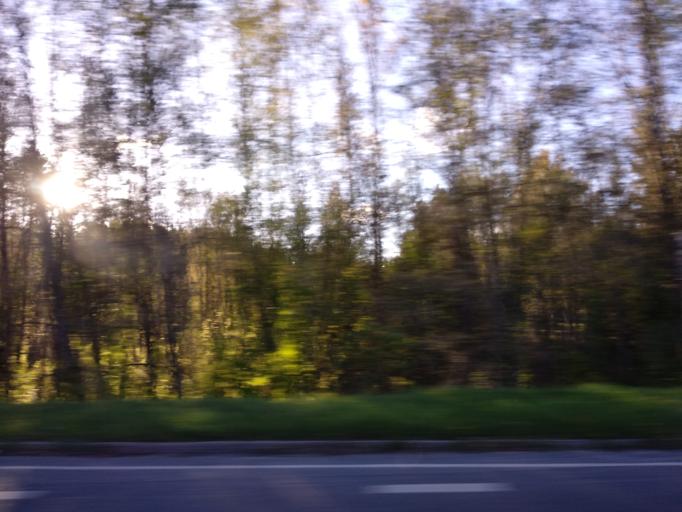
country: EE
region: Polvamaa
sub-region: Polva linn
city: Polva
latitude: 58.0439
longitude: 27.0657
